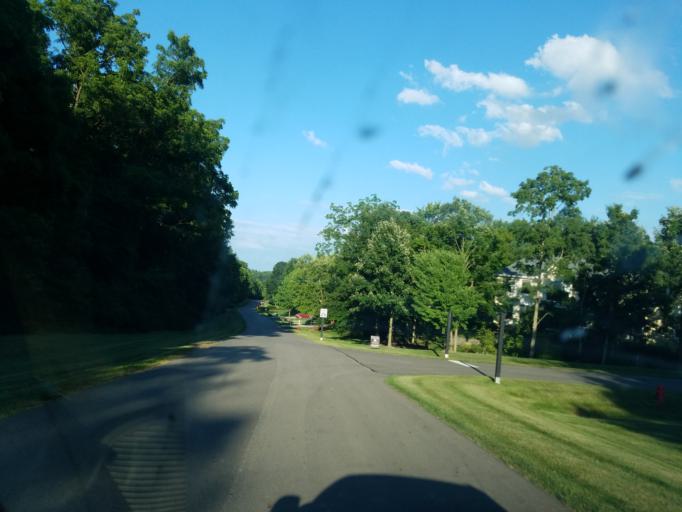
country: US
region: Ohio
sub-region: Delaware County
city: Powell
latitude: 40.1733
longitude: -83.0524
